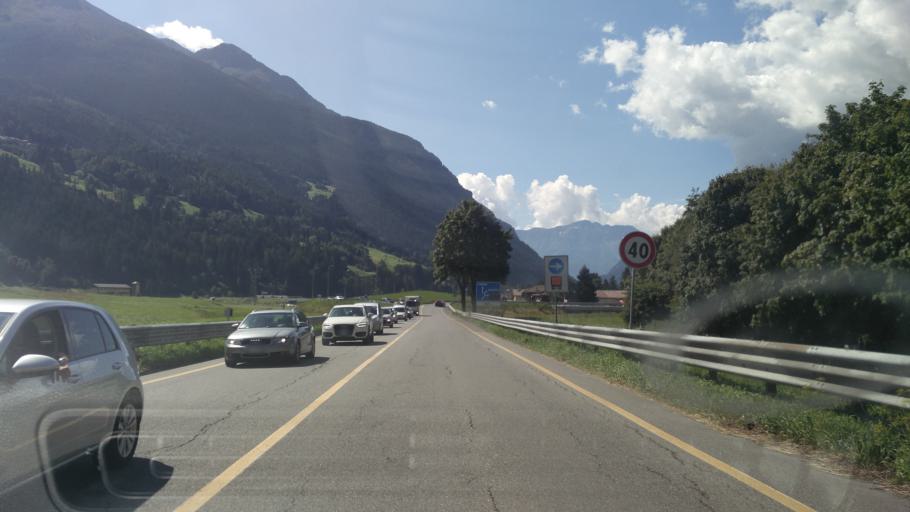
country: IT
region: Lombardy
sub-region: Provincia di Sondrio
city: Bormio
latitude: 46.4551
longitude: 10.3598
